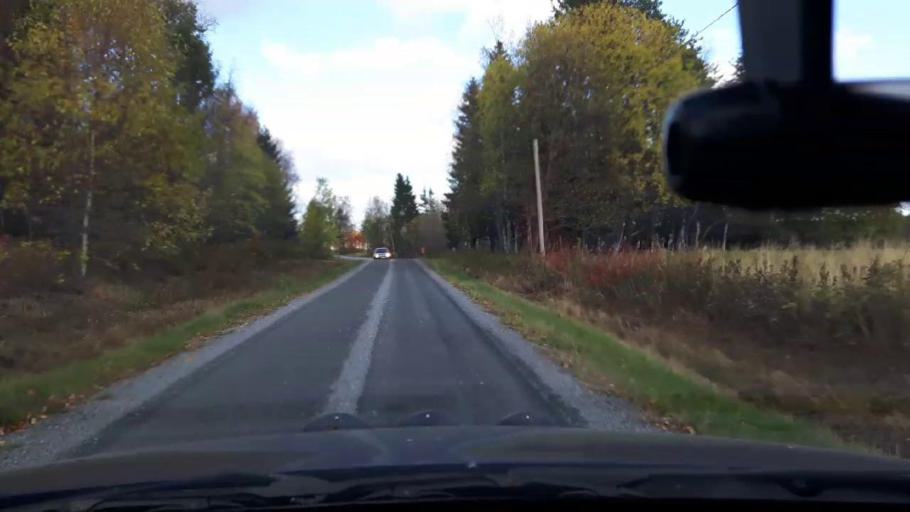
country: SE
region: Jaemtland
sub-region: Bergs Kommun
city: Hoverberg
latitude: 63.0549
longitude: 14.2389
